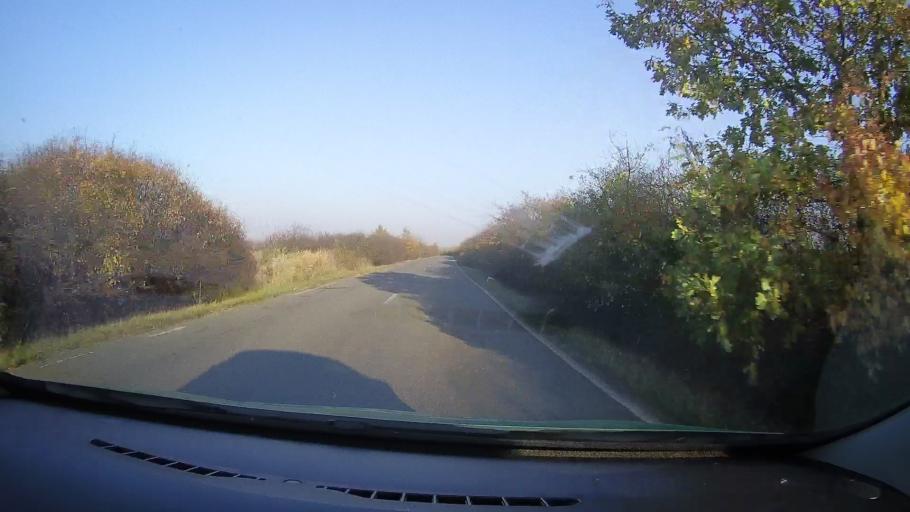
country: RO
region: Arad
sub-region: Comuna Tarnova
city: Chier
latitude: 46.3311
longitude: 21.8559
